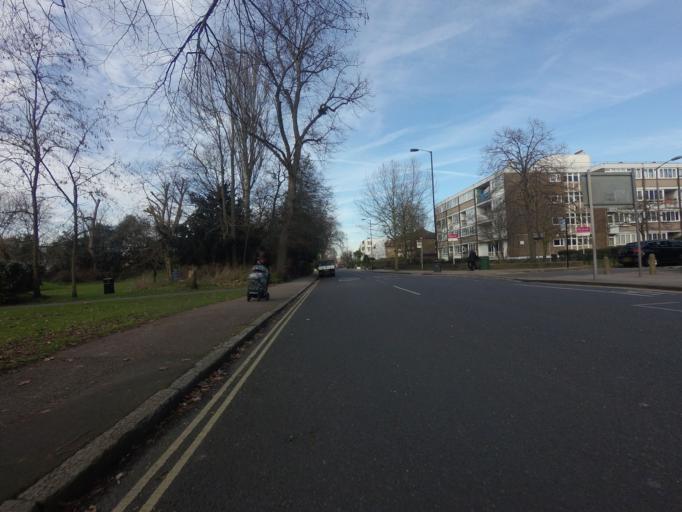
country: GB
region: England
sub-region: Greater London
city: Camberwell
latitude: 51.4633
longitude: -0.0651
